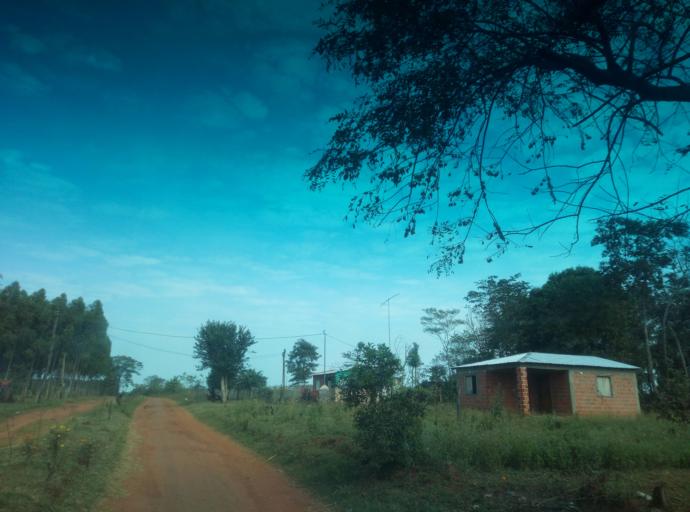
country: PY
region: Caaguazu
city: Carayao
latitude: -25.1903
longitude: -56.2519
